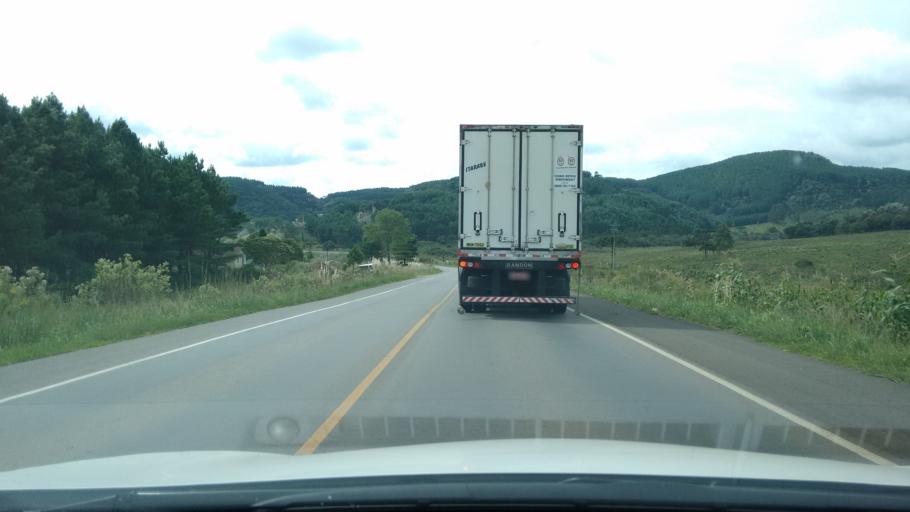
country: BR
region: Santa Catarina
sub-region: Otacilio Costa
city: Otacilio Costa
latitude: -27.3089
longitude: -50.2400
